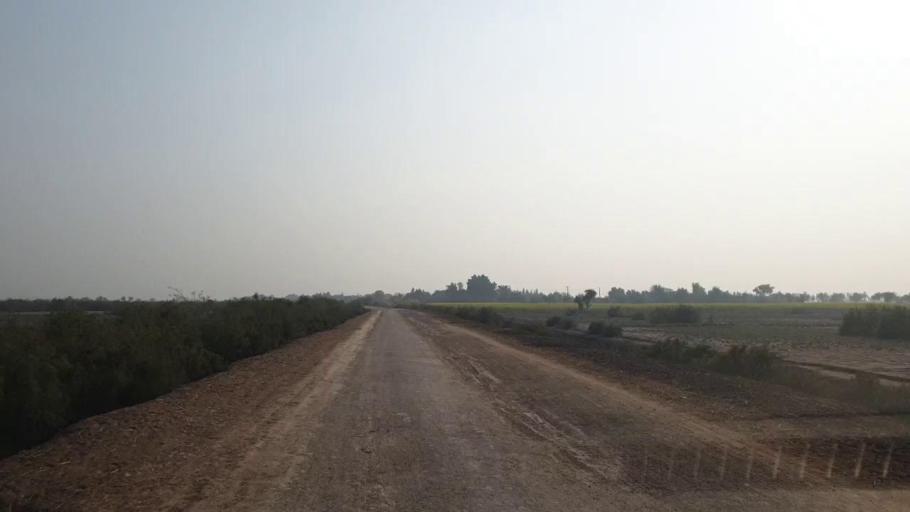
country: PK
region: Sindh
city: Shahdadpur
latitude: 25.9712
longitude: 68.5221
